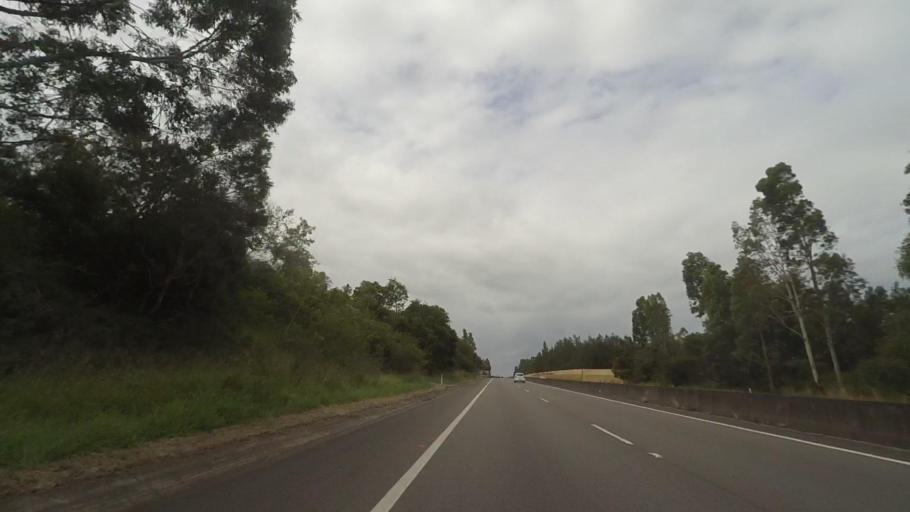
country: AU
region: New South Wales
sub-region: Port Stephens Shire
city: Raymond Terrace
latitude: -32.7652
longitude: 151.7632
